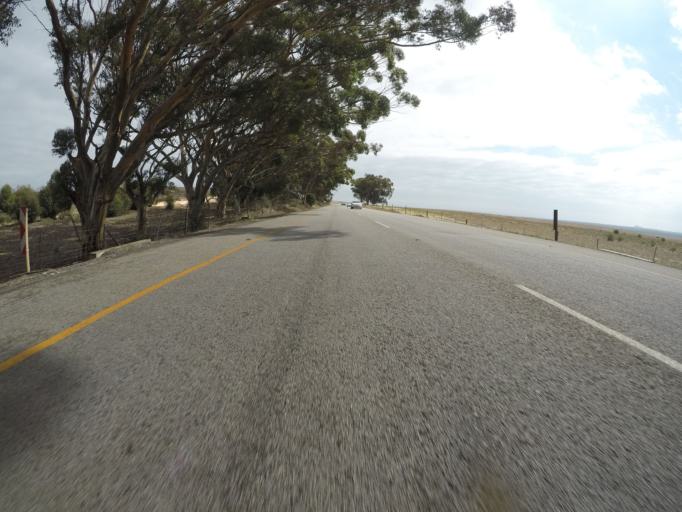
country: ZA
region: Western Cape
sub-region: City of Cape Town
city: Sunset Beach
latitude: -33.7230
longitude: 18.5031
